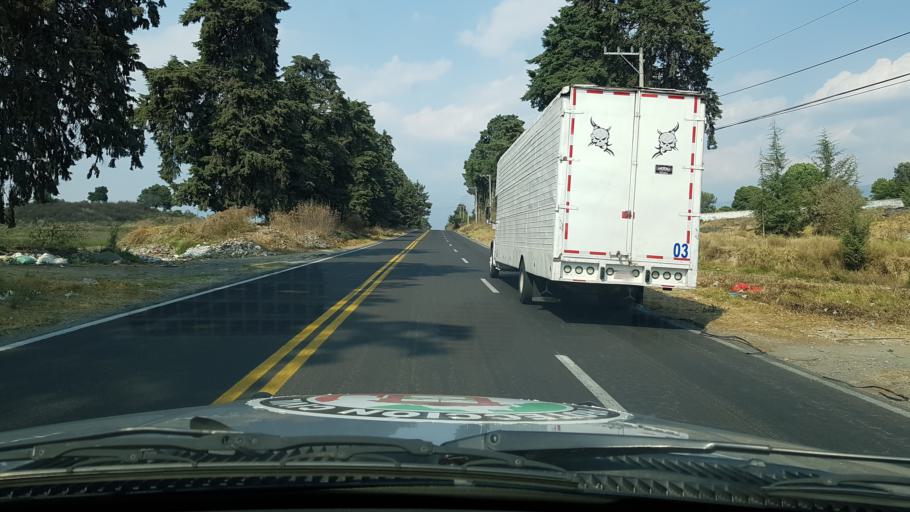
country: MX
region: Mexico
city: Ozumba de Alzate
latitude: 19.0395
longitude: -98.8053
